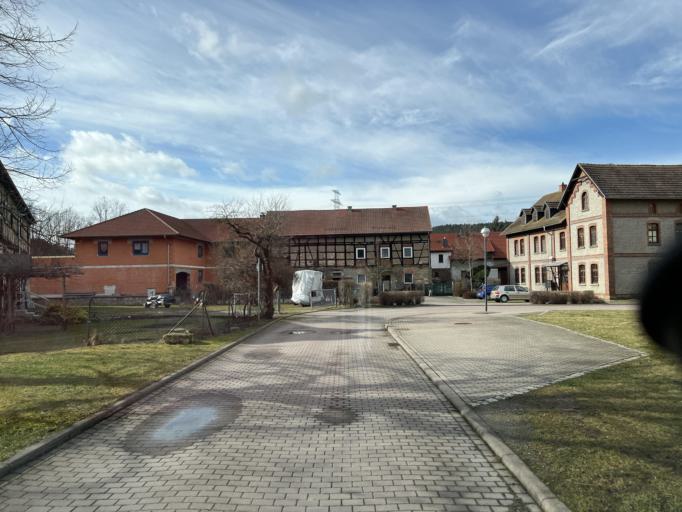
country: DE
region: Thuringia
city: Behringen
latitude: 50.7723
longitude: 11.0134
